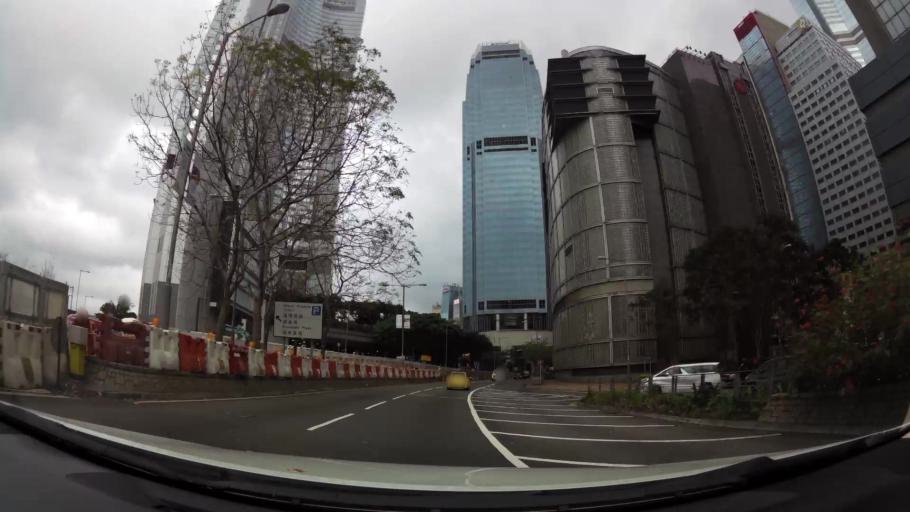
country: HK
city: Hong Kong
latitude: 22.2868
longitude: 114.1555
